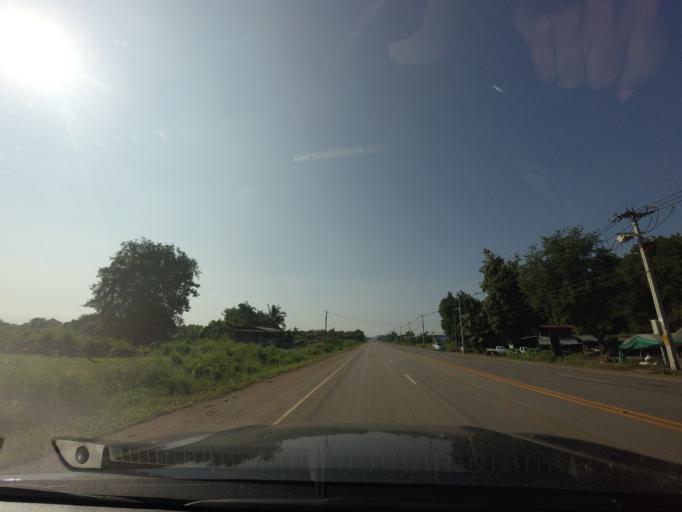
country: TH
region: Phetchabun
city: Lom Sak
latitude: 16.8219
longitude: 101.1814
